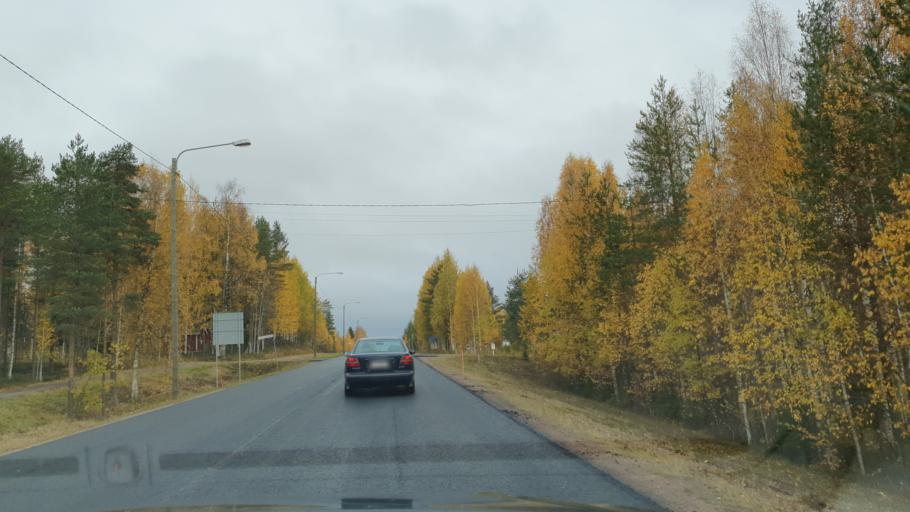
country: FI
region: Lapland
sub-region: Rovaniemi
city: Rovaniemi
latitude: 66.6511
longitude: 25.4529
